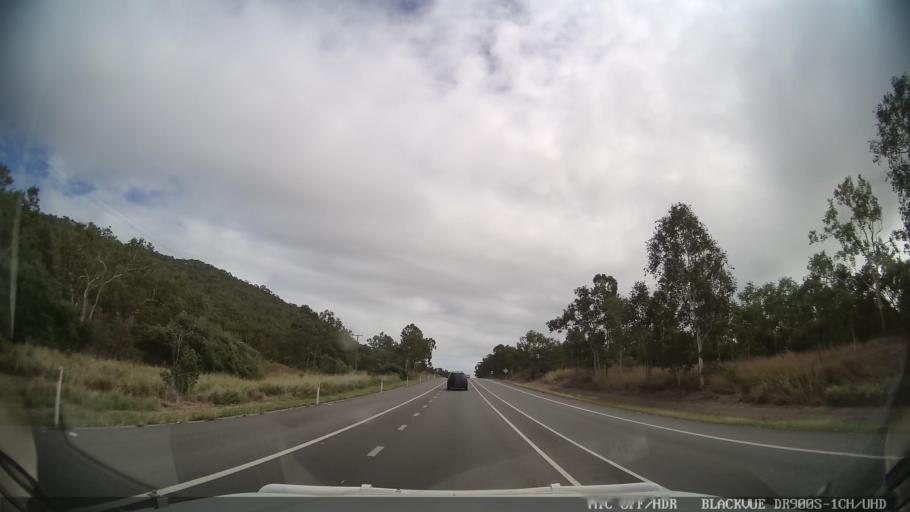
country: AU
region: Queensland
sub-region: Townsville
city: Townsville
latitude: -19.3671
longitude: 146.8922
